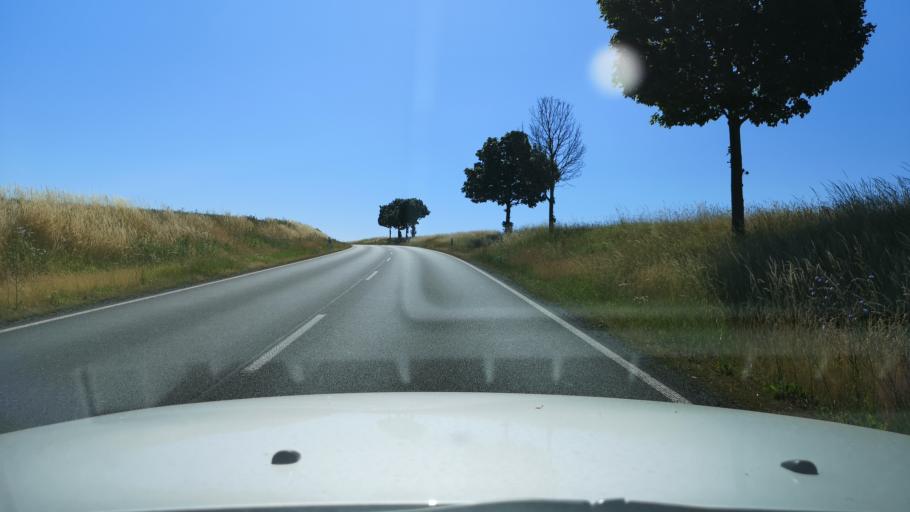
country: DE
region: Thuringia
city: Birkenhugel
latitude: 50.4442
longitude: 11.7751
